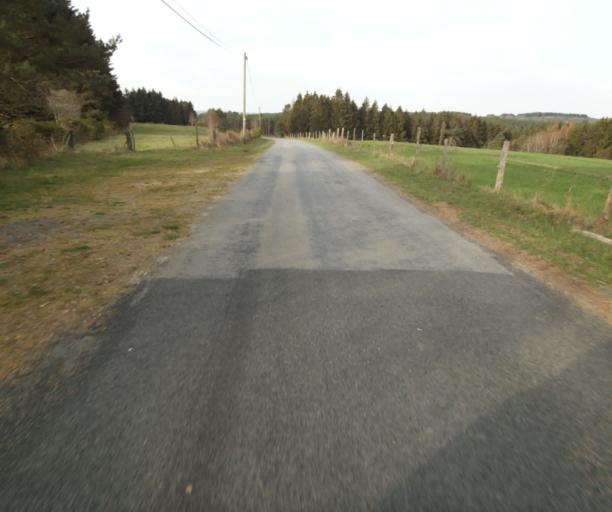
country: FR
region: Limousin
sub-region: Departement de la Correze
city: Treignac
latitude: 45.4654
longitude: 1.8179
